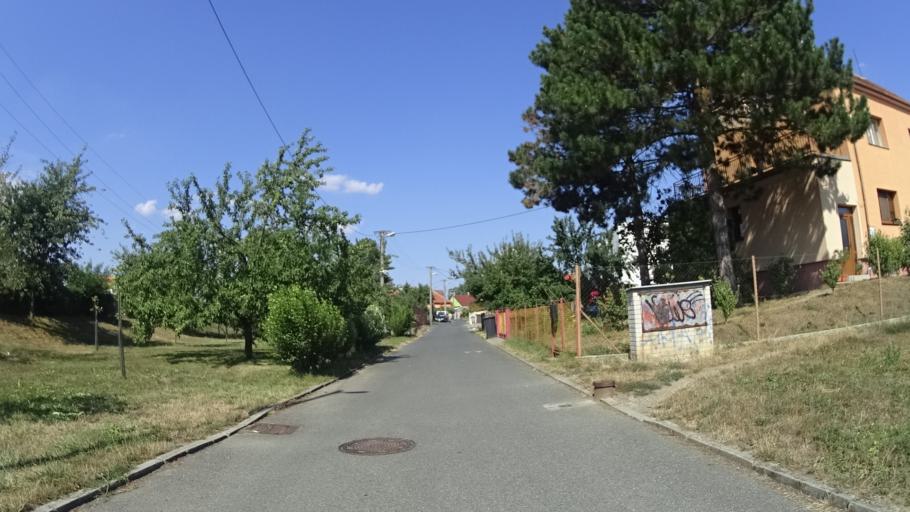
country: CZ
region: Zlin
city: Uhersky Ostroh
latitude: 48.9883
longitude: 17.3959
